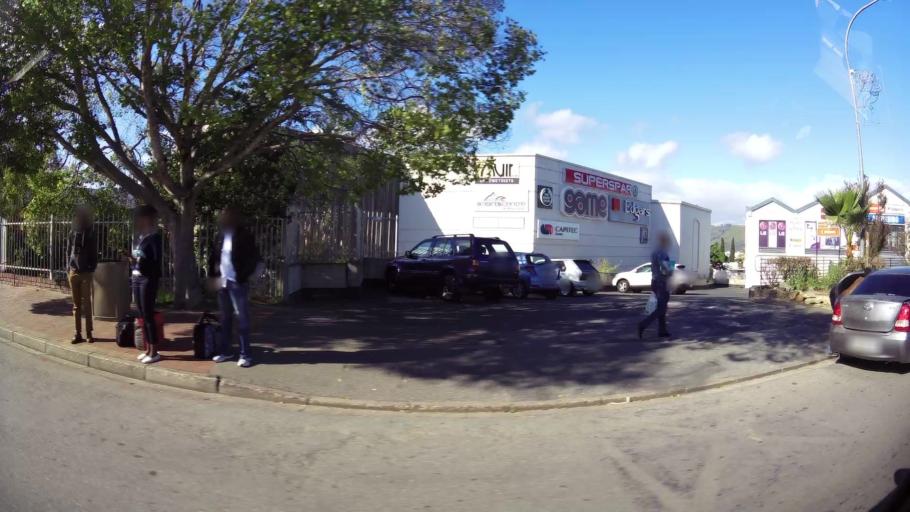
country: ZA
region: Western Cape
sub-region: Eden District Municipality
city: Knysna
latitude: -34.0350
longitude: 23.0433
